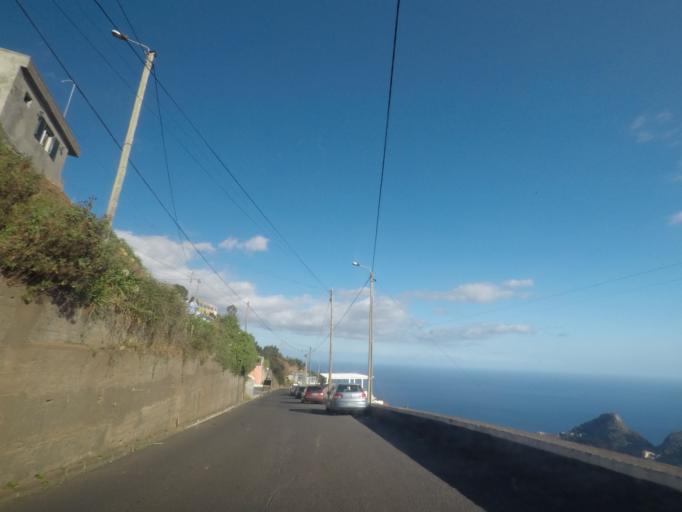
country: PT
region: Madeira
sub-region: Ribeira Brava
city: Campanario
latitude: 32.6659
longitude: -16.9982
